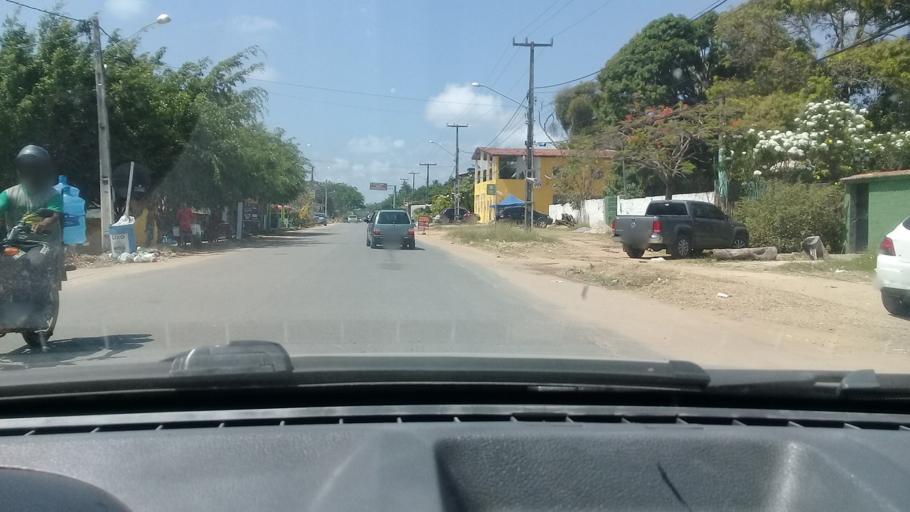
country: BR
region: Pernambuco
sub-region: Itamaraca
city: Itamaraca
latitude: -7.7874
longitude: -34.8404
